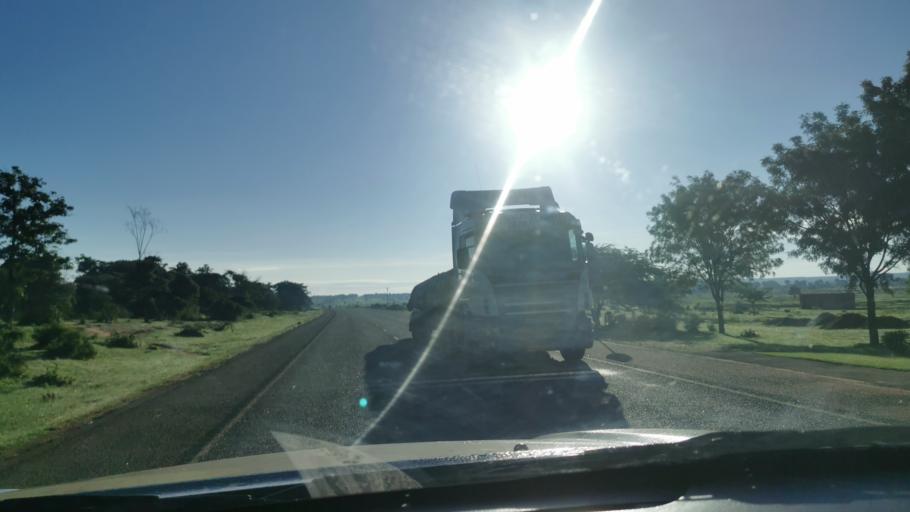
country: TZ
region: Shinyanga
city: Kahama
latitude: -3.8392
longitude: 32.6423
